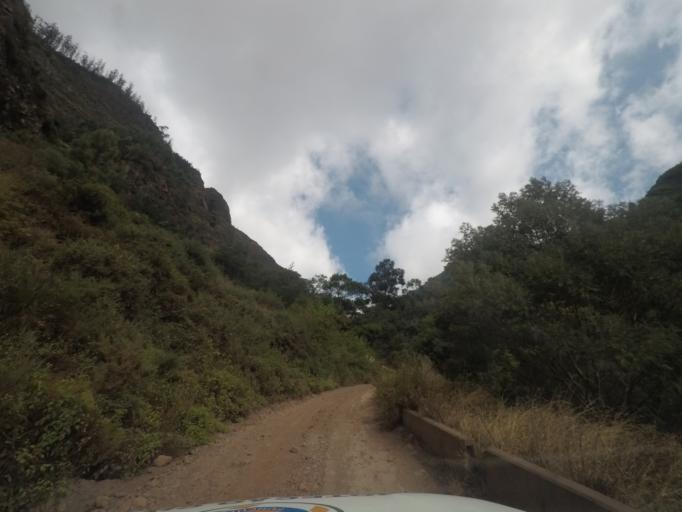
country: PT
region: Madeira
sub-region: Funchal
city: Nossa Senhora do Monte
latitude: 32.6903
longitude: -16.9175
